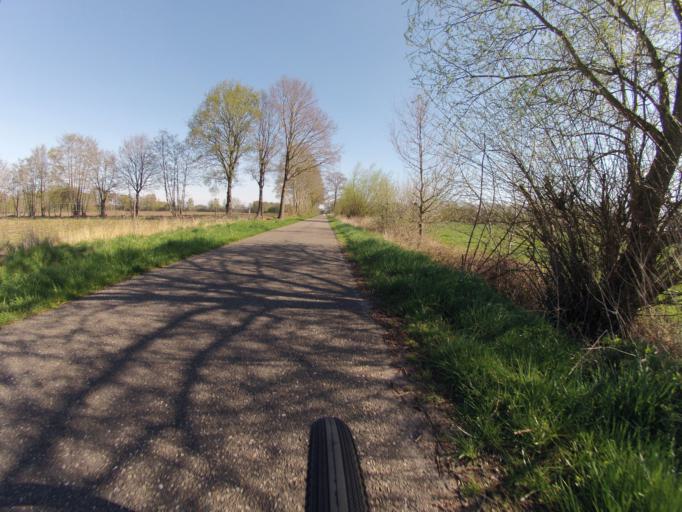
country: DE
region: Lower Saxony
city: Isterberg
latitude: 52.3509
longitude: 7.1637
